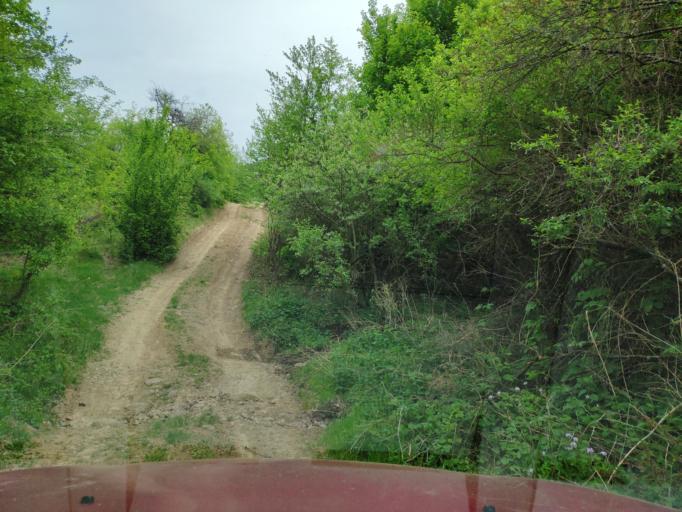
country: SK
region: Banskobystricky
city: Revuca
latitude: 48.5175
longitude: 20.1408
